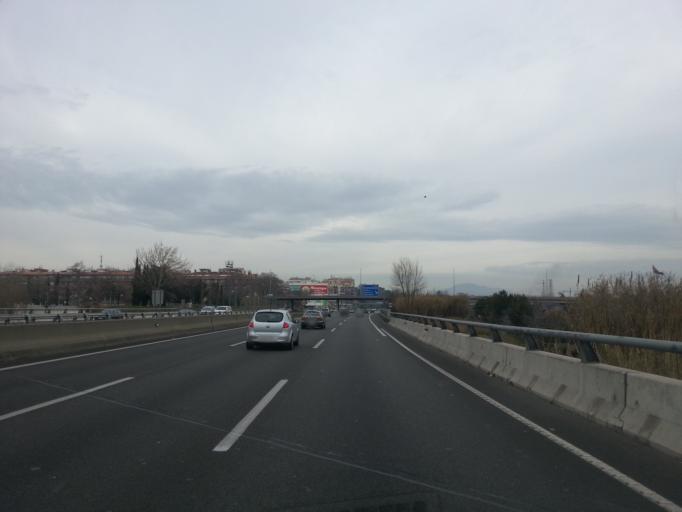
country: ES
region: Catalonia
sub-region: Provincia de Barcelona
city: Ripollet
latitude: 41.4911
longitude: 2.1546
